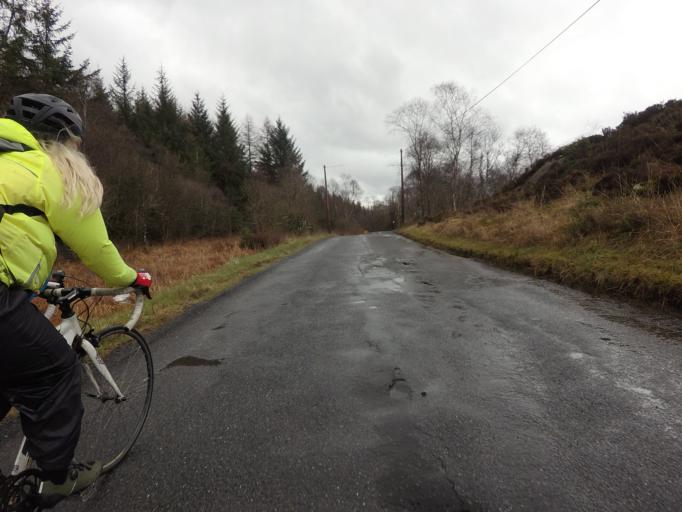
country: GB
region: Scotland
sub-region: West Dunbartonshire
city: Balloch
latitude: 56.1998
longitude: -4.5266
